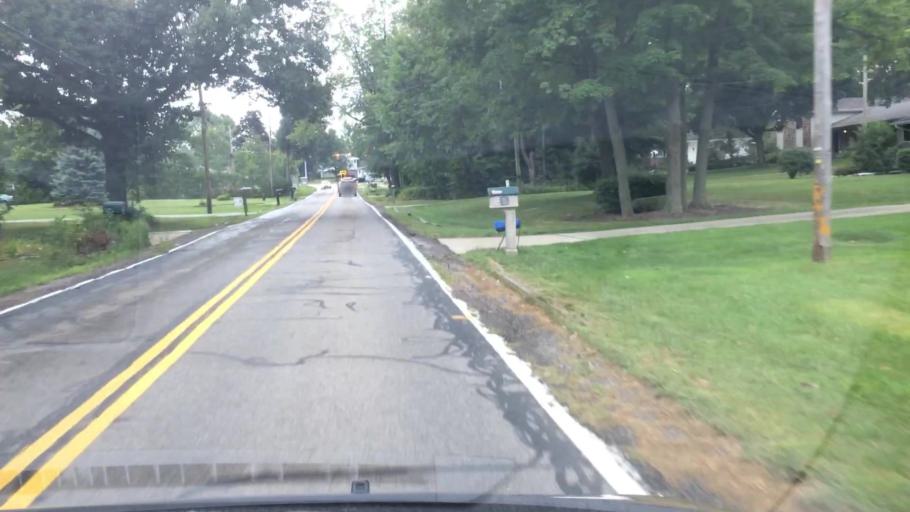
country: US
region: Ohio
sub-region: Cuyahoga County
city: Strongsville
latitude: 41.2776
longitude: -81.8110
